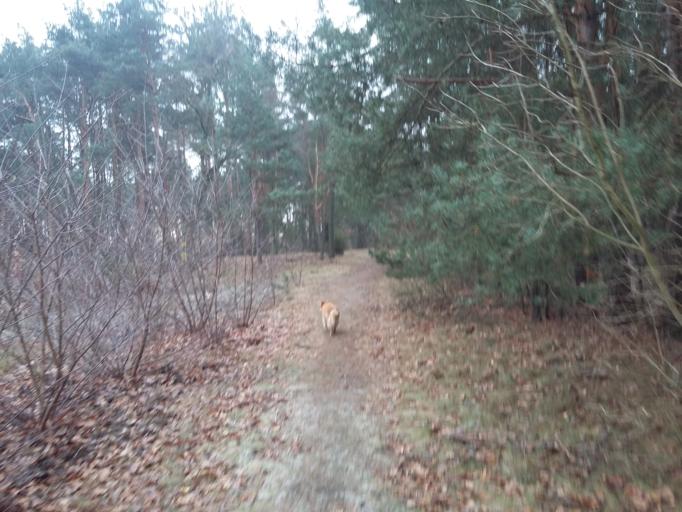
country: PL
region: Lodz Voivodeship
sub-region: Powiat pabianicki
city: Ksawerow
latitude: 51.7239
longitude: 19.3849
